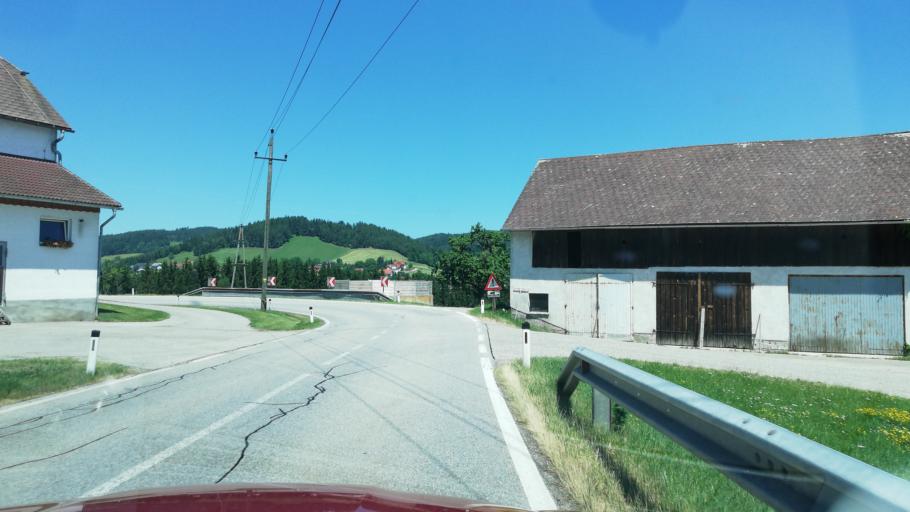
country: AT
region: Upper Austria
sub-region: Politischer Bezirk Urfahr-Umgebung
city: Haibach im Muhlkreis
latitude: 48.4434
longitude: 14.3593
